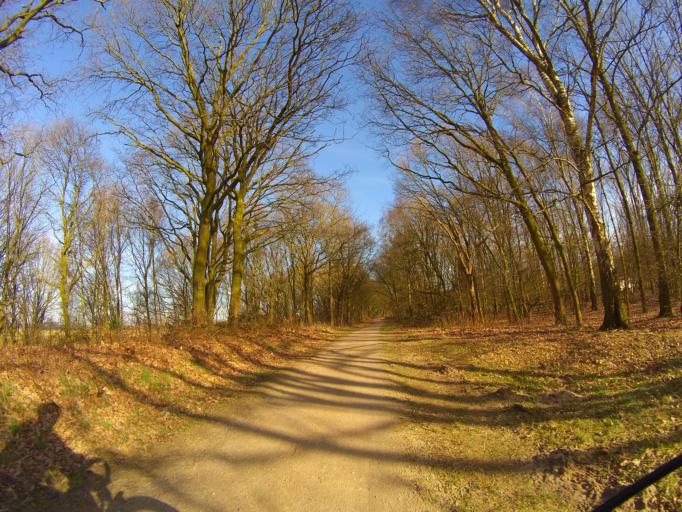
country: NL
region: North Holland
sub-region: Gemeente Huizen
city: Huizen
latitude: 52.3099
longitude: 5.2342
